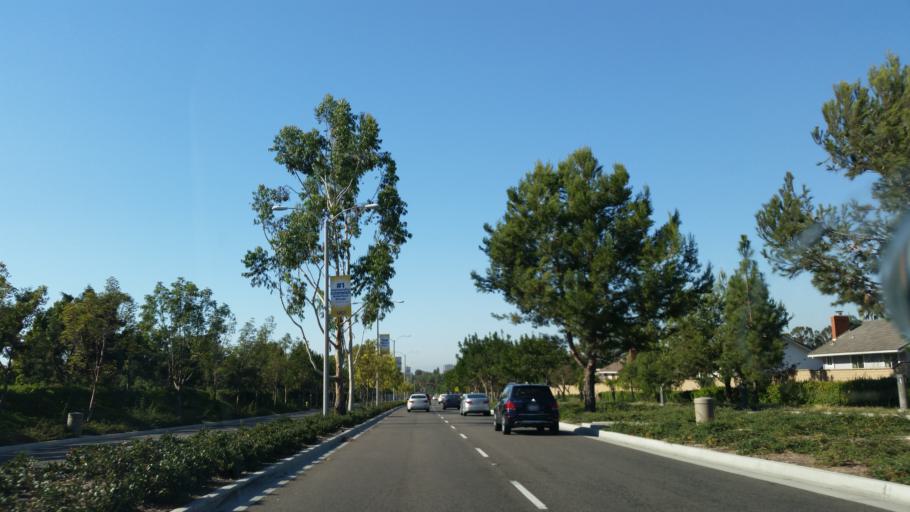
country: US
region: California
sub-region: Orange County
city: Irvine
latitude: 33.6475
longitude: -117.8231
